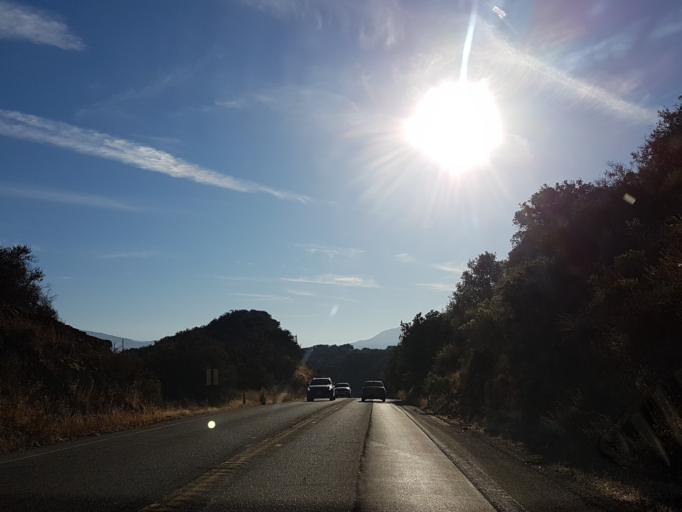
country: US
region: California
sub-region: Santa Barbara County
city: Santa Ynez
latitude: 34.5625
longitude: -119.9296
